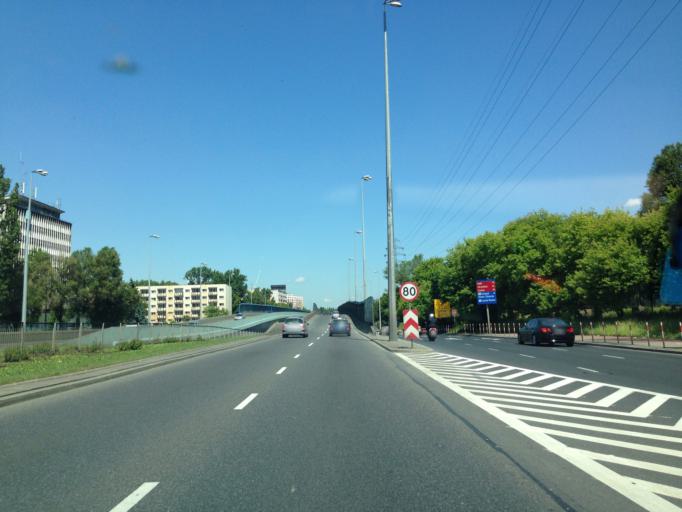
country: PL
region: Masovian Voivodeship
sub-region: Warszawa
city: Ochota
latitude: 52.2260
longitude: 20.9578
